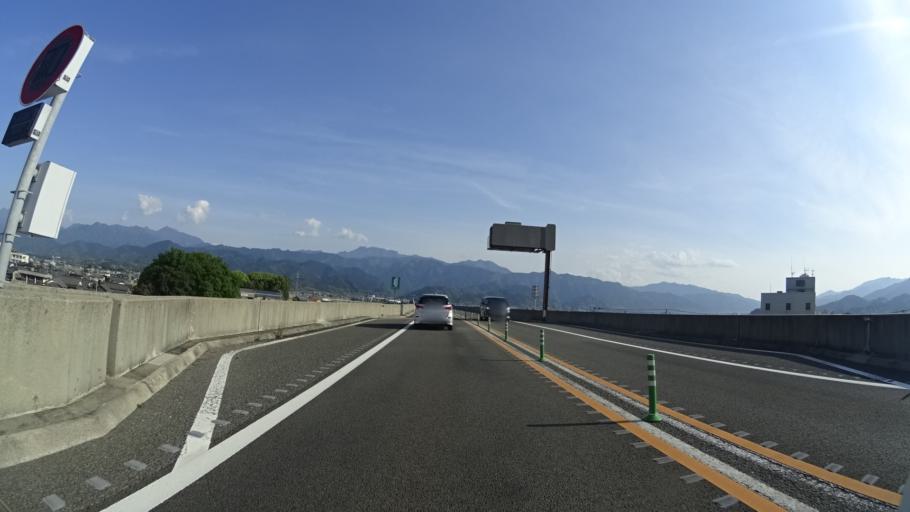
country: JP
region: Ehime
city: Saijo
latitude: 33.9133
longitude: 133.0728
